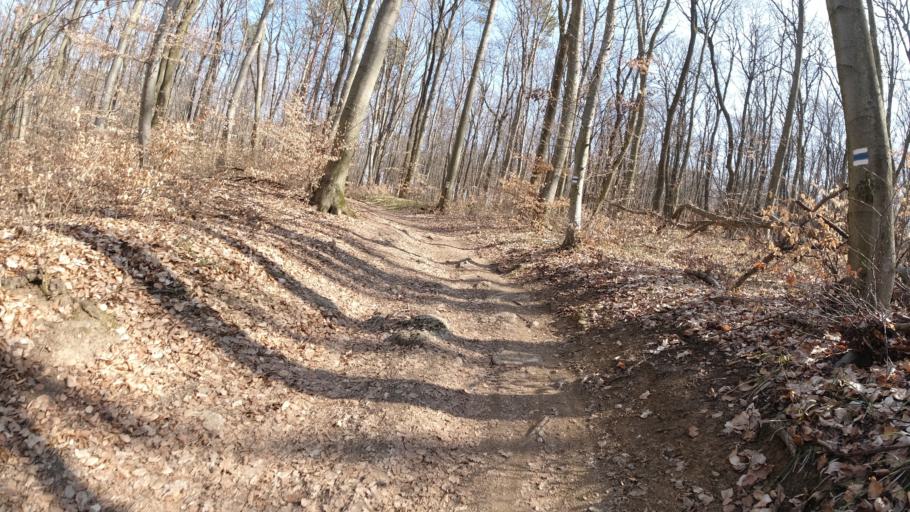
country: SK
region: Trnavsky
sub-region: Okres Trnava
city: Piestany
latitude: 48.5621
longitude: 17.8691
